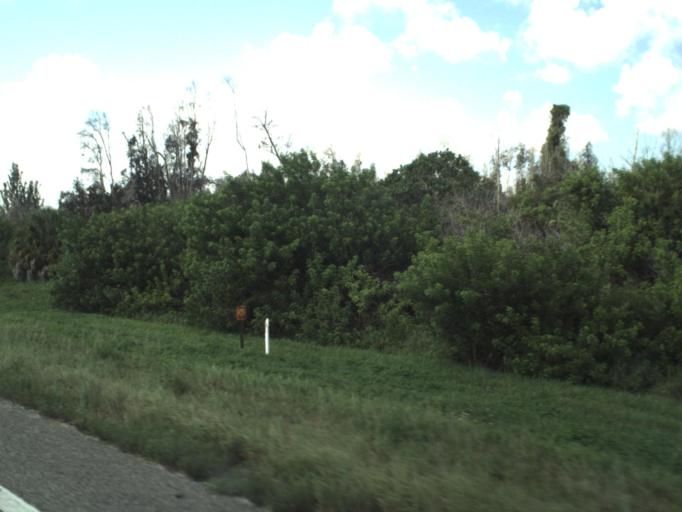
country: US
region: Florida
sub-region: Broward County
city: Weston
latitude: 26.0505
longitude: -80.4340
